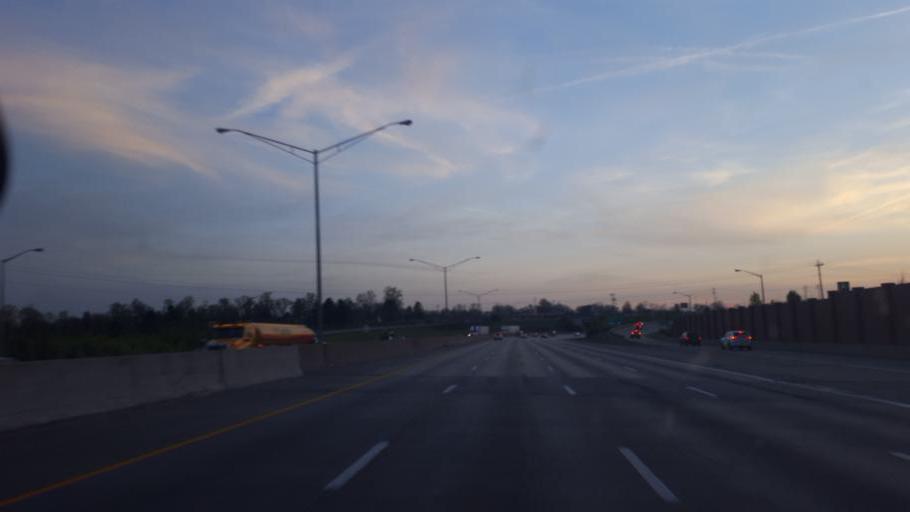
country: US
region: Kentucky
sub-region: Kenton County
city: Fort Mitchell
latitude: 39.0533
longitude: -84.5473
